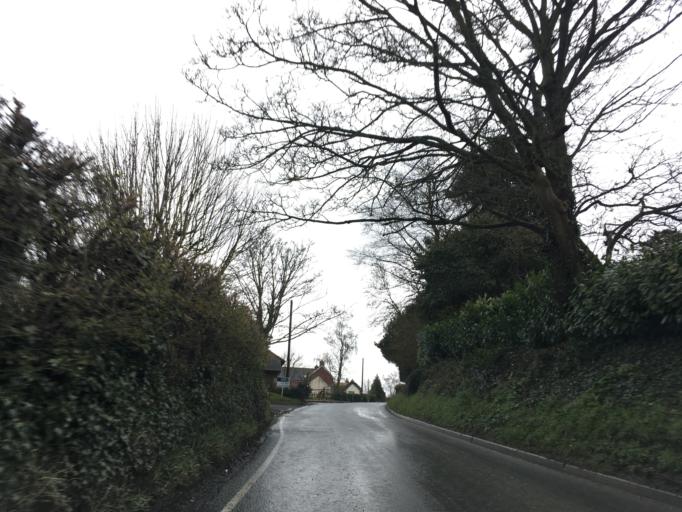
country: GB
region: England
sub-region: Borough of Swindon
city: Wanborough
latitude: 51.5424
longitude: -1.7055
